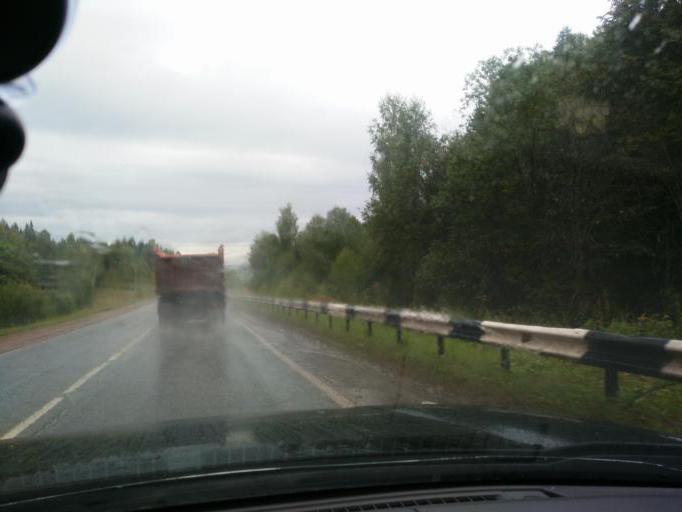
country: RU
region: Perm
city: Kultayevo
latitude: 57.8427
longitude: 55.8276
